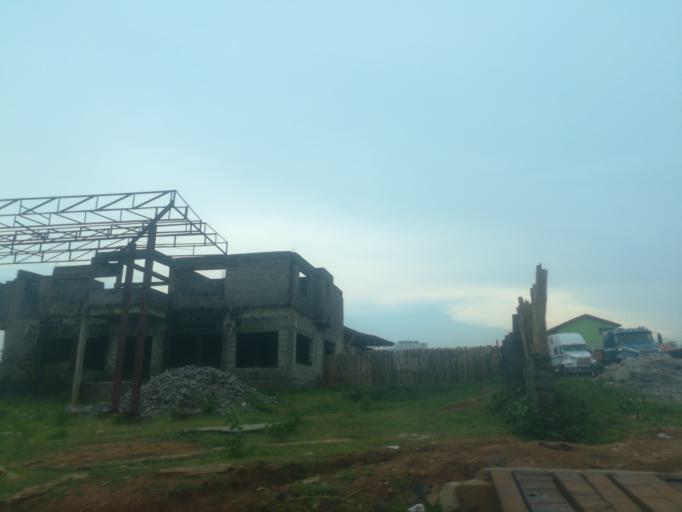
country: NG
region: Oyo
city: Ibadan
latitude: 7.3537
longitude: 3.8194
